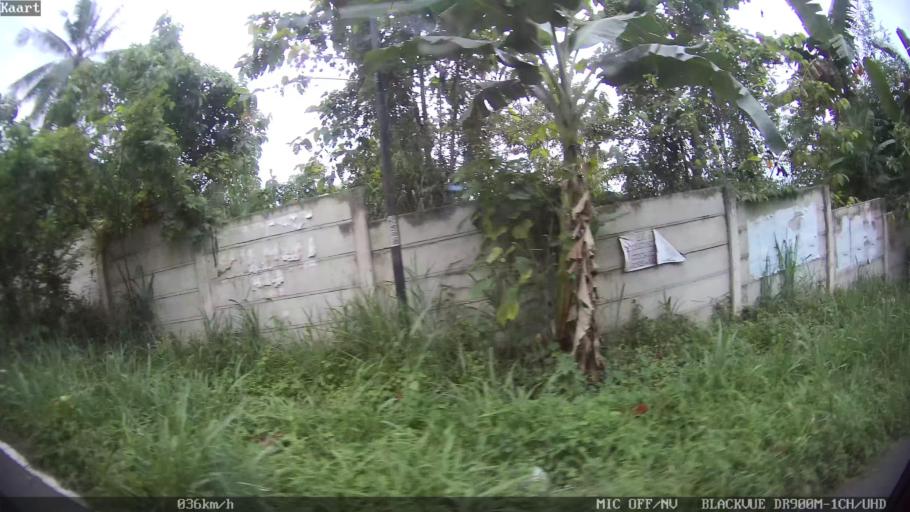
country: ID
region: Lampung
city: Bandarlampung
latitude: -5.4255
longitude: 105.2343
